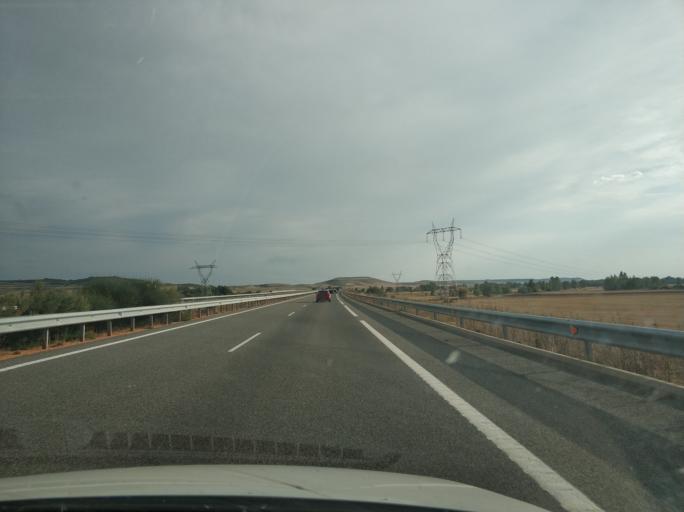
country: ES
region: Castille and Leon
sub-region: Provincia de Burgos
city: Sotragero
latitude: 42.4241
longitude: -3.6954
